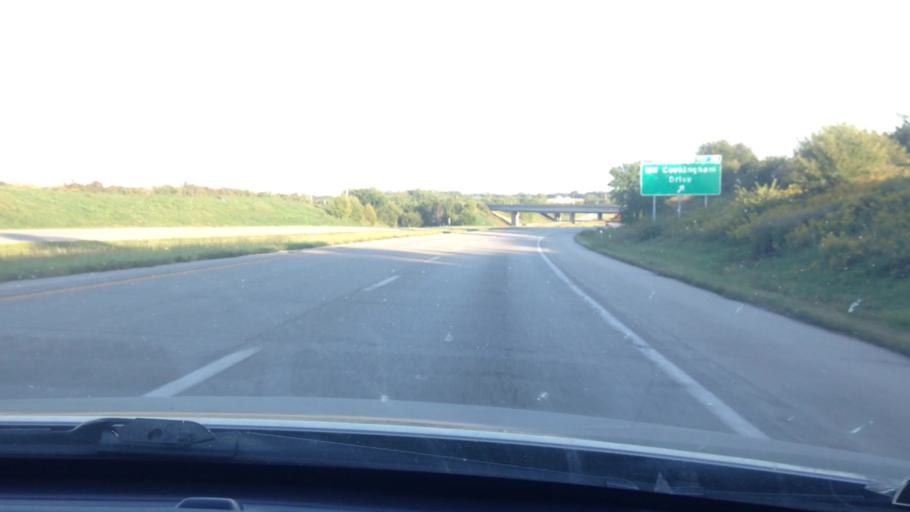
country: US
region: Missouri
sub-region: Platte County
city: Weatherby Lake
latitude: 39.3145
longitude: -94.6776
